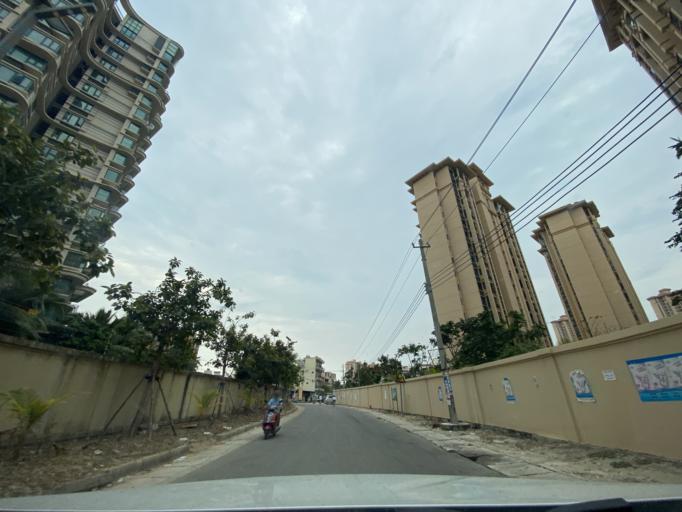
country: CN
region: Hainan
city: Yingzhou
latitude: 18.3971
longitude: 109.8435
